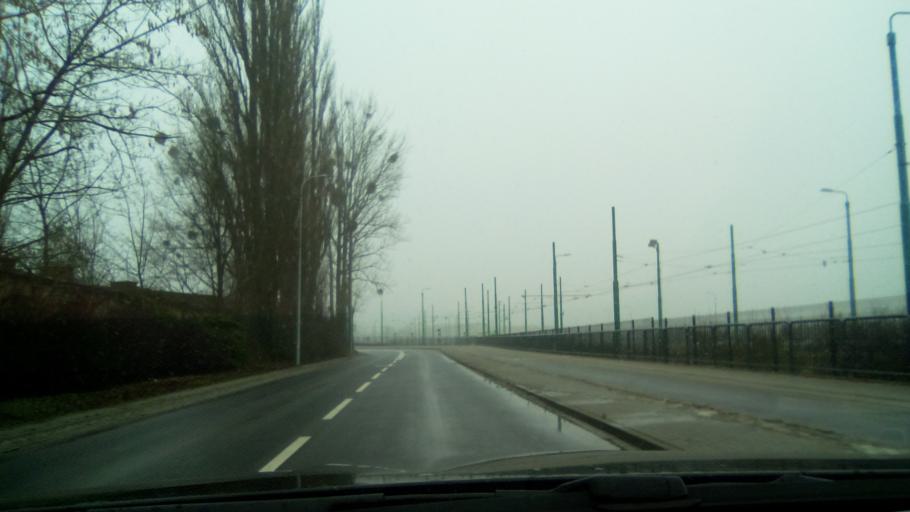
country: PL
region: Greater Poland Voivodeship
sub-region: Poznan
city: Poznan
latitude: 52.3831
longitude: 17.0069
